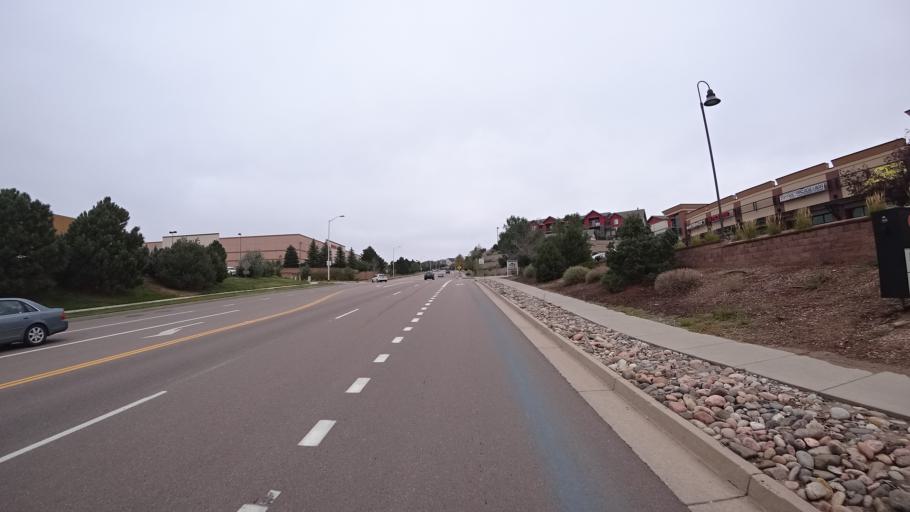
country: US
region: Colorado
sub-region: El Paso County
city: Cimarron Hills
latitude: 38.8951
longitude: -104.7153
